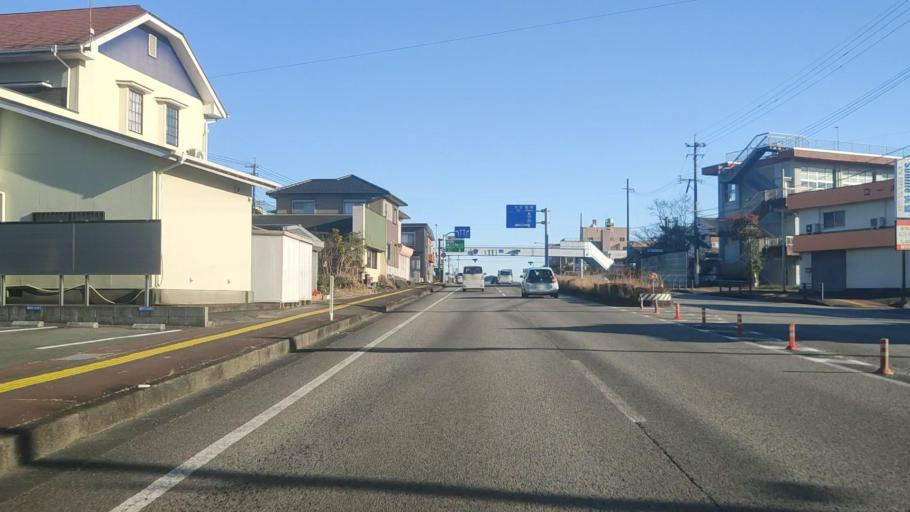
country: JP
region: Miyazaki
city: Nobeoka
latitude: 32.4716
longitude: 131.6509
